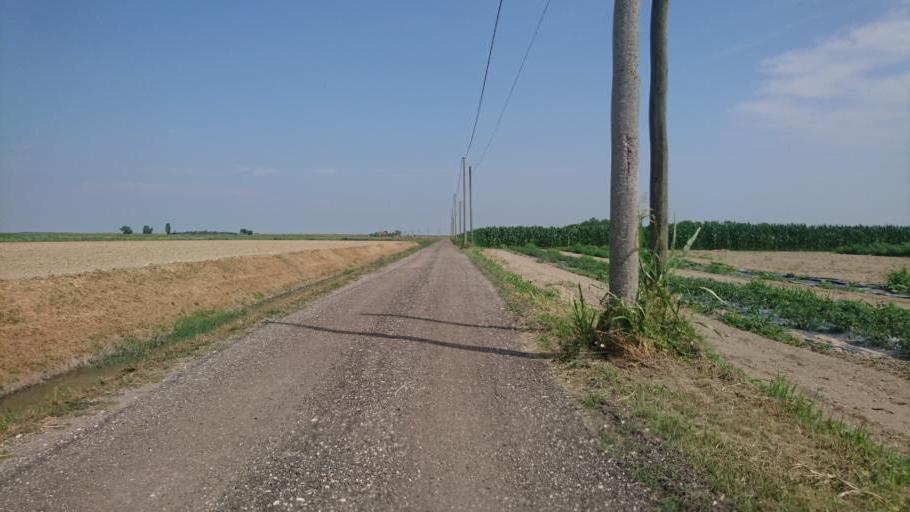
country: IT
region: Veneto
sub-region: Provincia di Venezia
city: Valli
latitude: 45.2506
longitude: 12.1929
